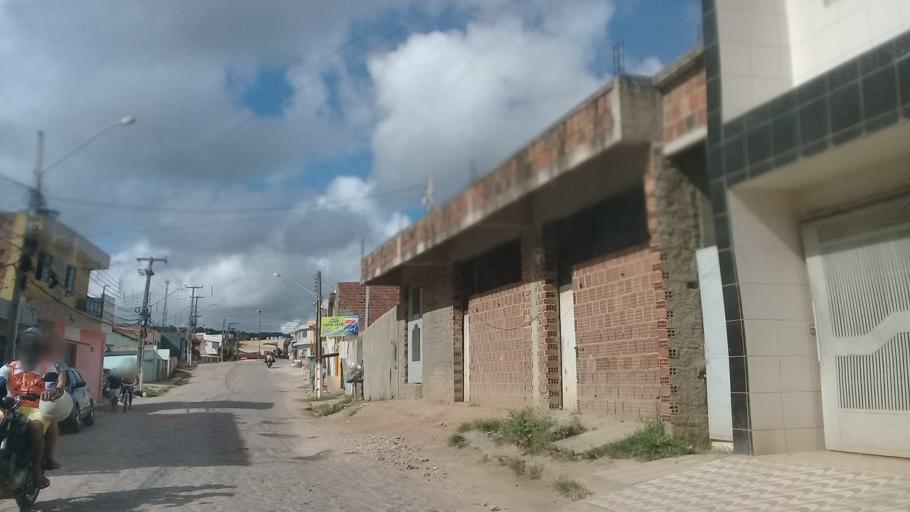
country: BR
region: Pernambuco
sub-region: Vitoria De Santo Antao
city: Vitoria de Santo Antao
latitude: -8.1272
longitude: -35.2962
